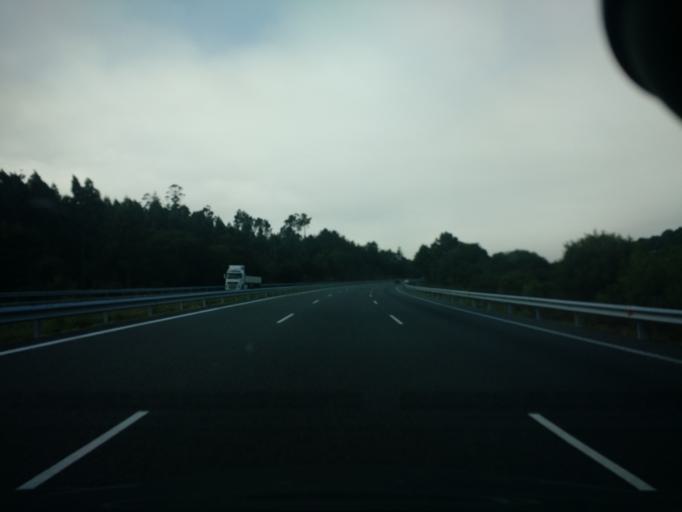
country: ES
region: Galicia
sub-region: Provincia da Coruna
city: Abegondo
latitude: 43.1812
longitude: -8.3108
